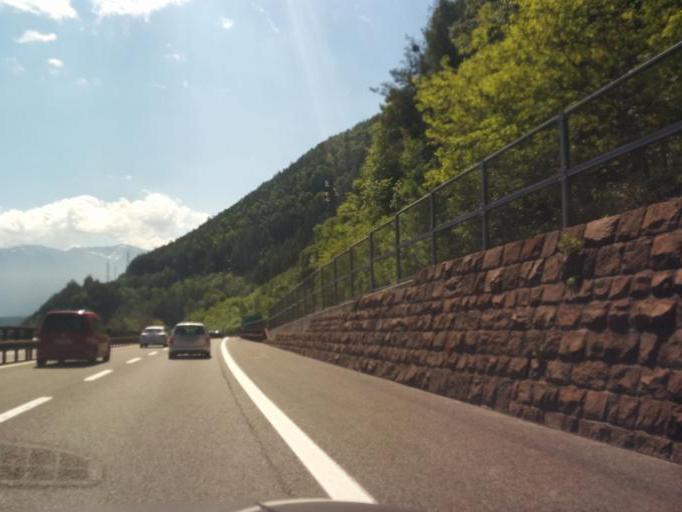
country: IT
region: Trentino-Alto Adige
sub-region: Bolzano
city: Fortezza
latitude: 46.7768
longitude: 11.6272
